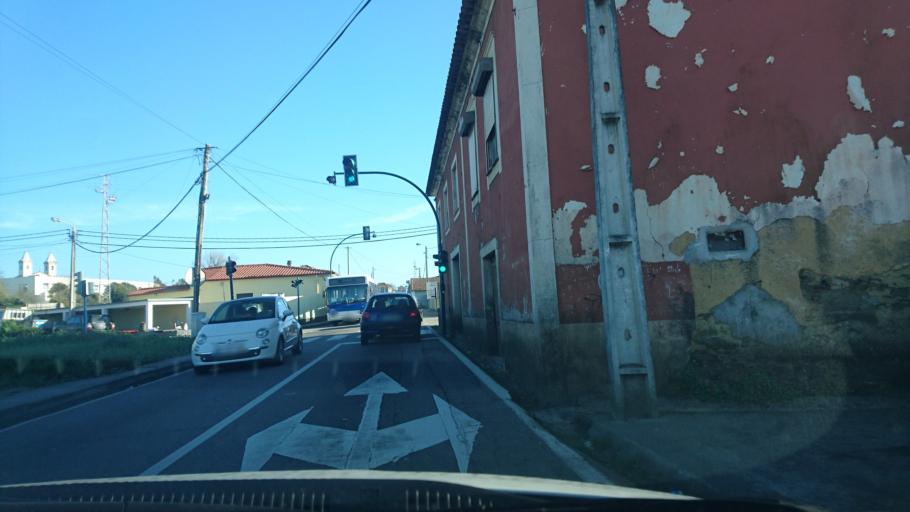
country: PT
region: Aveiro
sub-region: Espinho
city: Silvalde
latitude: 40.9935
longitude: -8.6313
